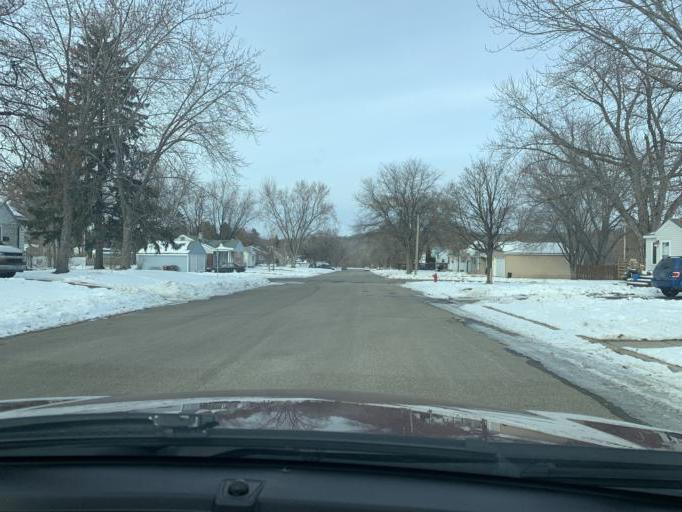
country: US
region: Minnesota
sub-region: Washington County
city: Saint Paul Park
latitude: 44.8381
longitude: -92.9785
